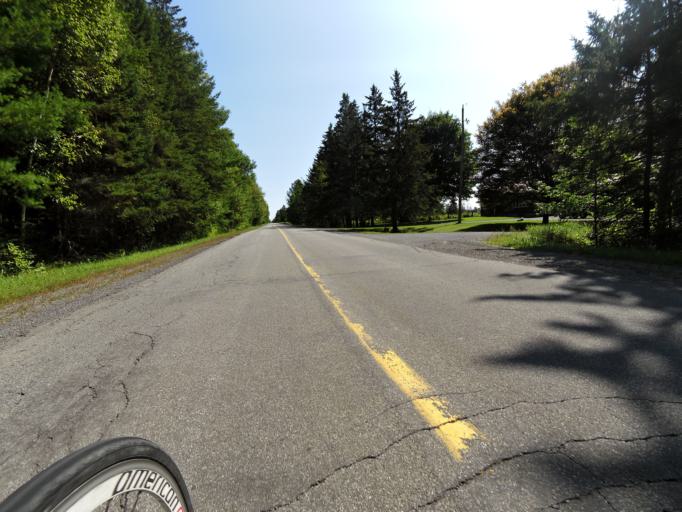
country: CA
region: Ontario
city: Arnprior
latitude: 45.4992
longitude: -76.1493
